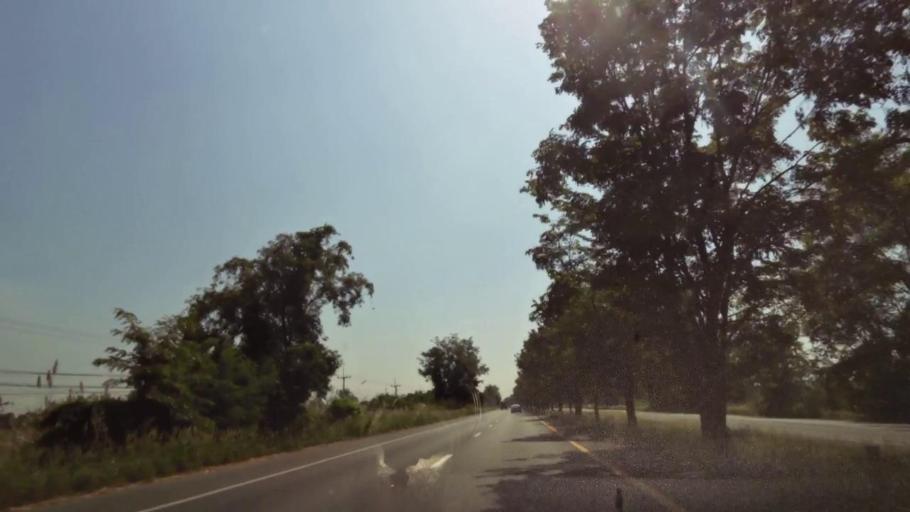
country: TH
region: Nakhon Sawan
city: Kao Liao
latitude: 15.9271
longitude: 100.1122
